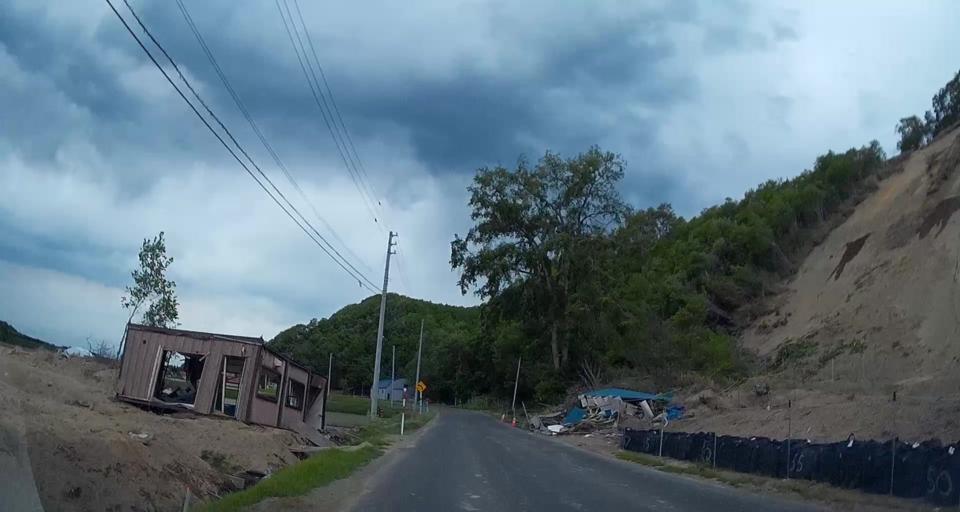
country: JP
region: Hokkaido
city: Chitose
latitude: 42.7591
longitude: 141.9628
